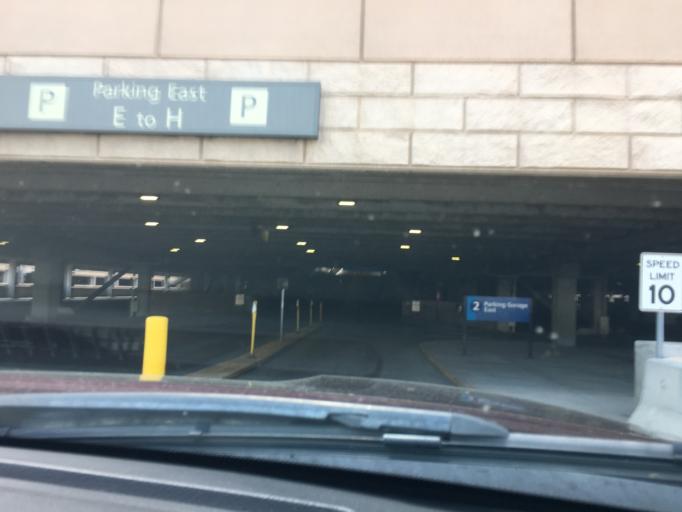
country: US
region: Colorado
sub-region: Weld County
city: Lochbuie
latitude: 39.8492
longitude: -104.6702
